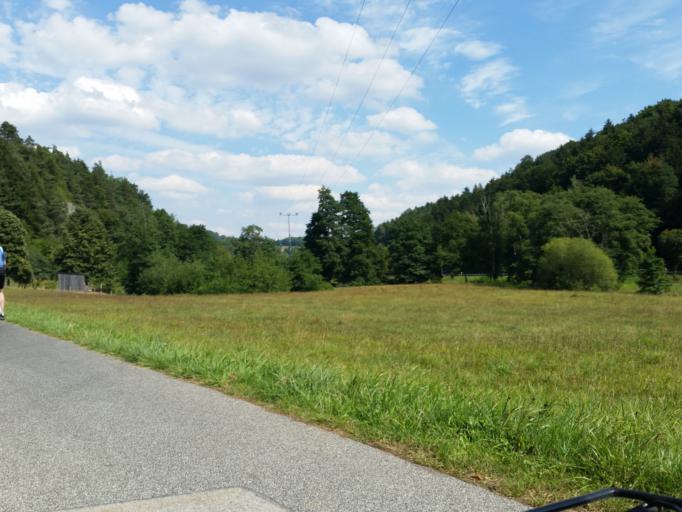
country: DE
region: Bavaria
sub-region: Upper Palatinate
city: Kastl
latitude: 49.3701
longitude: 11.6633
